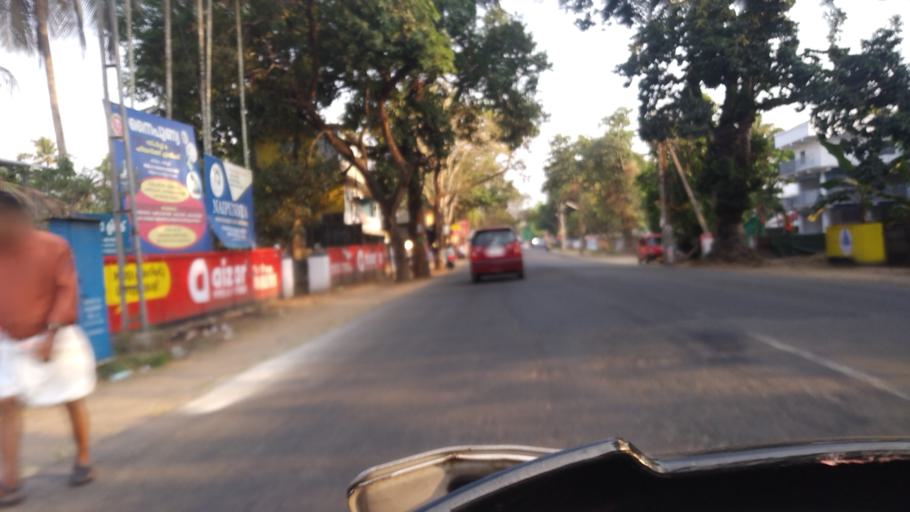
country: IN
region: Kerala
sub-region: Thrissur District
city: Thanniyam
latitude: 10.3810
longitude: 76.1215
